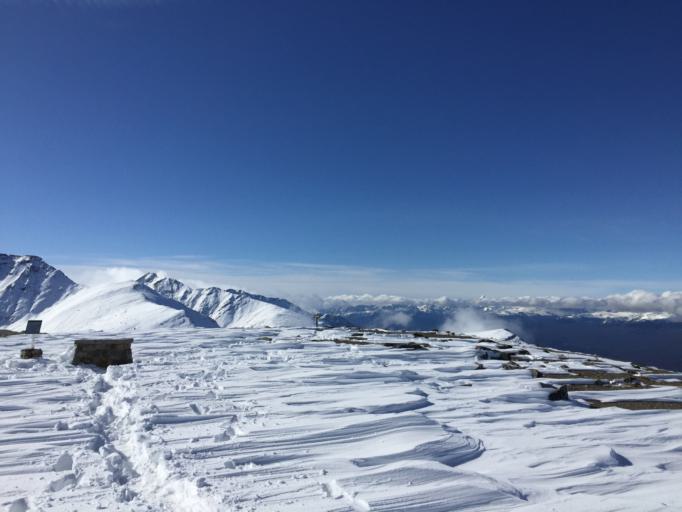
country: CA
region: Alberta
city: Jasper Park Lodge
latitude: 52.8269
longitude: -118.1330
